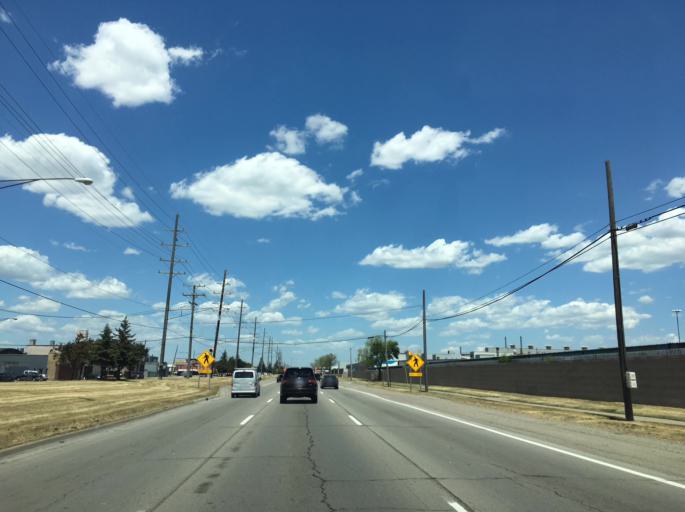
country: US
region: Michigan
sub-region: Macomb County
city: Warren
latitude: 42.4520
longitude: -83.0442
